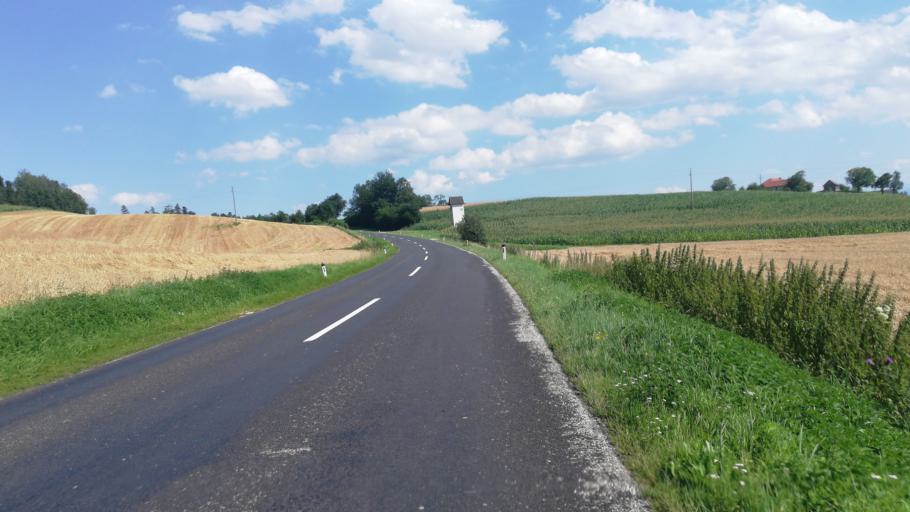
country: AT
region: Upper Austria
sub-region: Wels-Land
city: Gunskirchen
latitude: 48.1597
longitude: 13.9198
